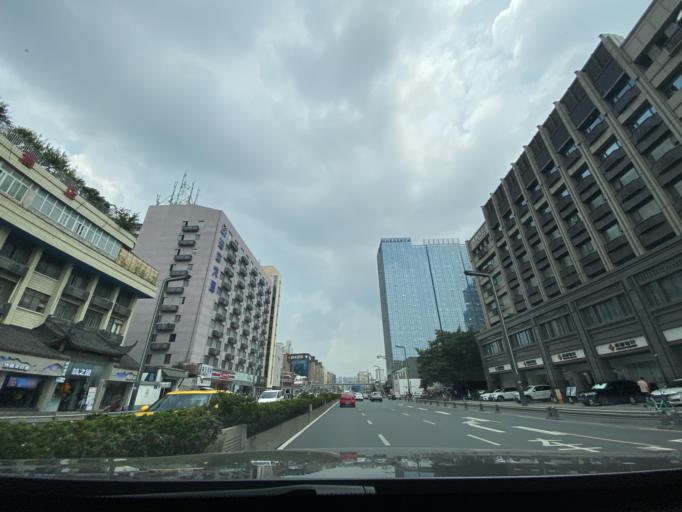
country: CN
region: Sichuan
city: Chengdu
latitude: 30.6309
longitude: 104.0740
